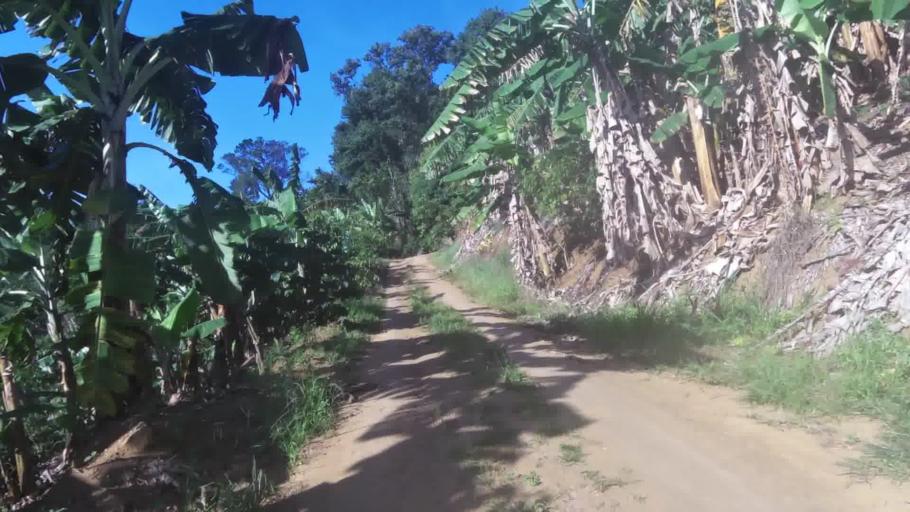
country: BR
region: Espirito Santo
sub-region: Iconha
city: Iconha
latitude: -20.7550
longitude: -40.8101
